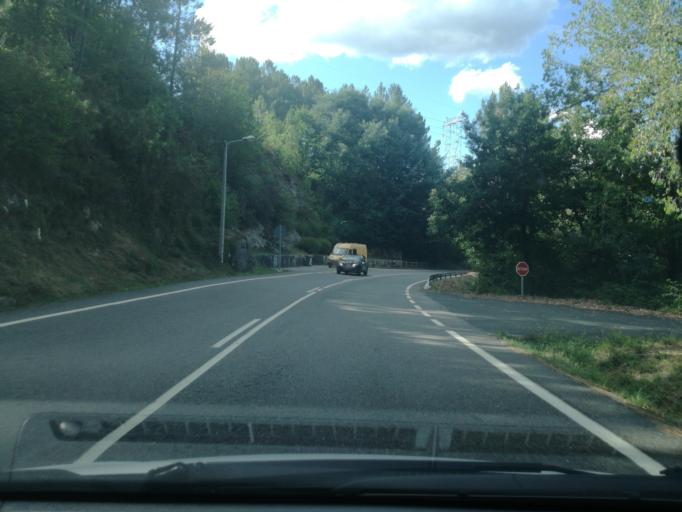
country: ES
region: Galicia
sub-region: Provincia de Ourense
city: Lobios
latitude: 41.9048
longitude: -8.0874
